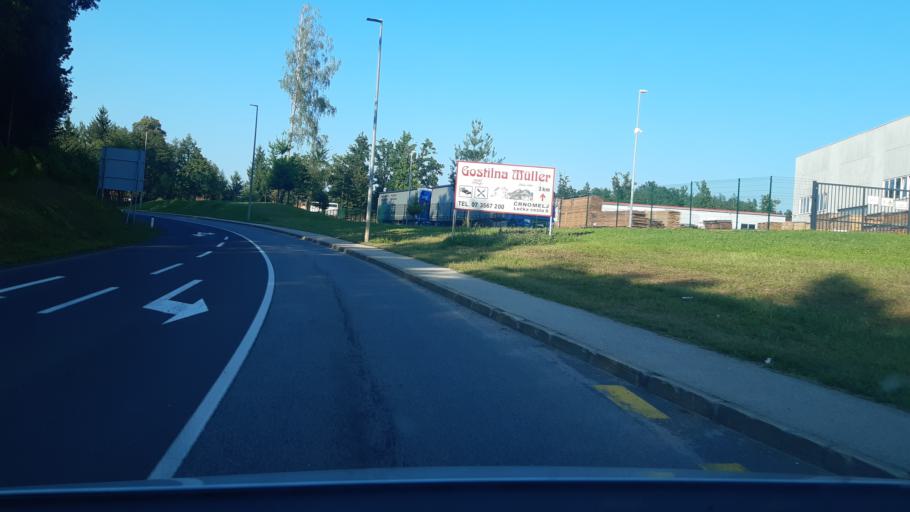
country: SI
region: Crnomelj
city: Crnomelj
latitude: 45.5575
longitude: 15.1680
